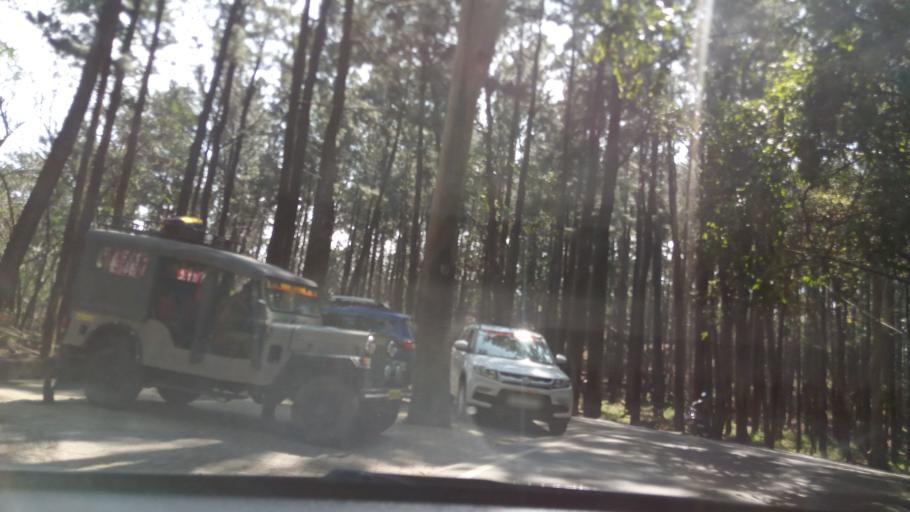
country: IN
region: Andhra Pradesh
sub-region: Chittoor
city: Tirumala
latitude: 13.6782
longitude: 79.3330
